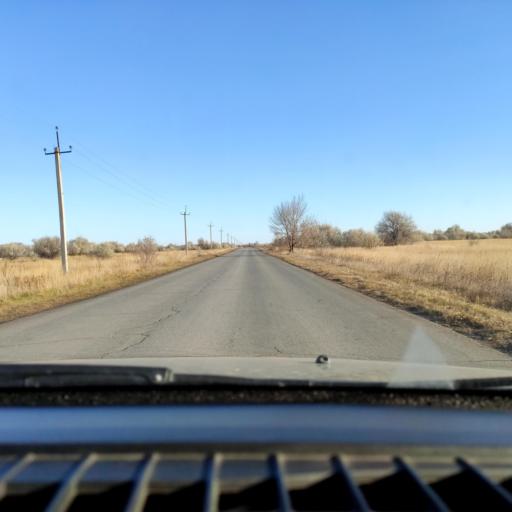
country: RU
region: Samara
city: Tol'yatti
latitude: 53.6511
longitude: 49.3235
